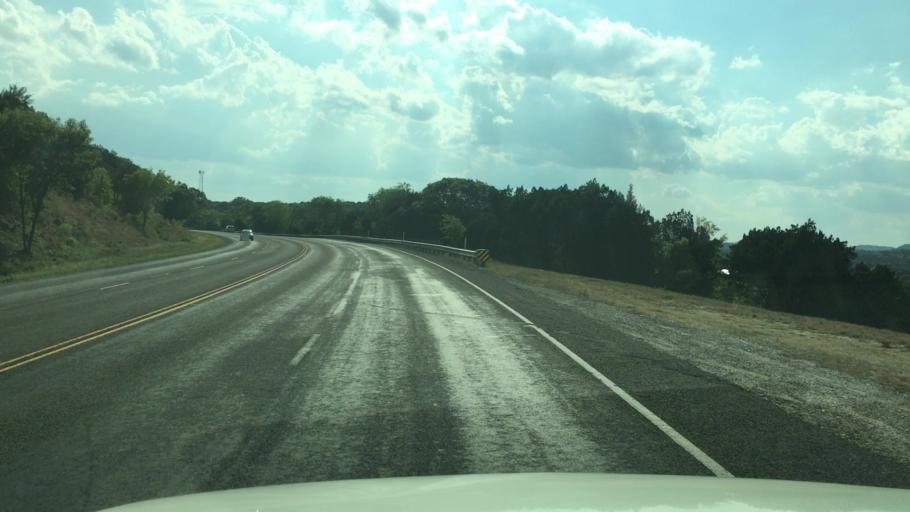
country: US
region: Texas
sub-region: Blanco County
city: Johnson City
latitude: 30.2022
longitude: -98.3496
